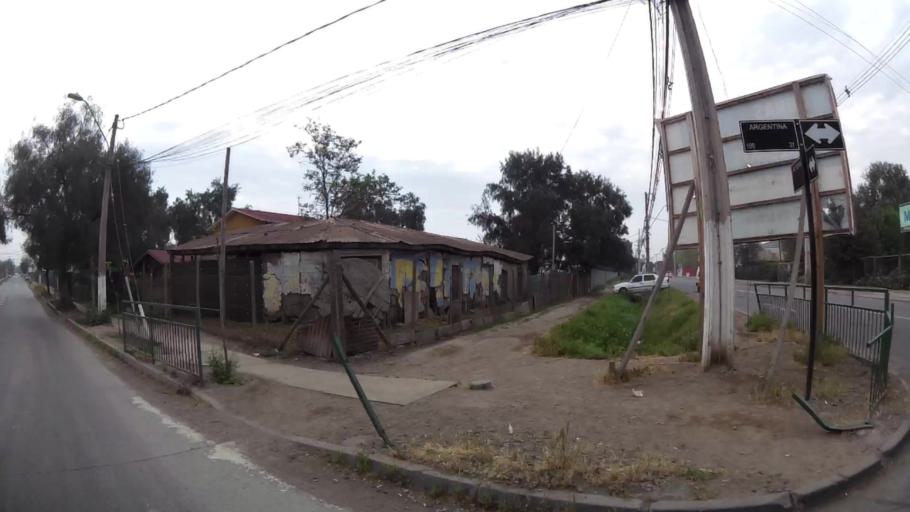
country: CL
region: Santiago Metropolitan
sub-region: Provincia de Chacabuco
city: Lampa
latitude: -33.2390
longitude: -70.8110
